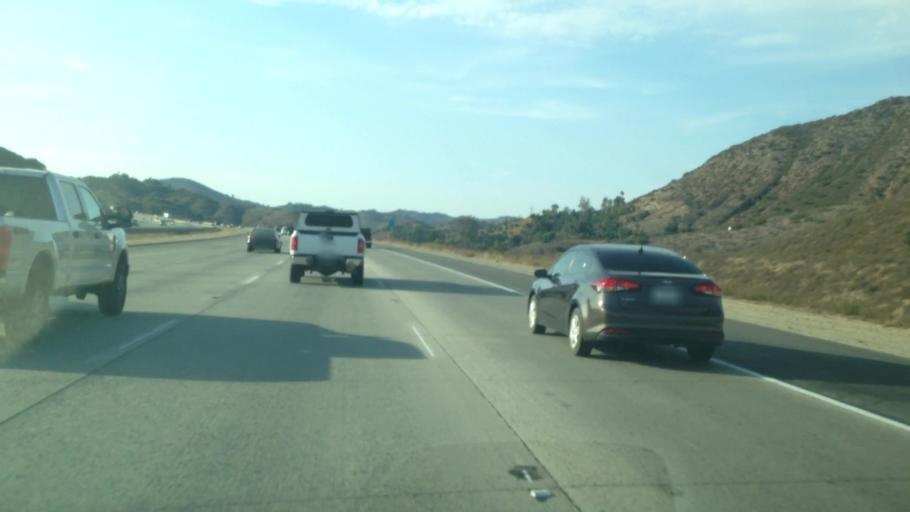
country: US
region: California
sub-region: San Diego County
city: Rainbow
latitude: 33.3595
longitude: -117.1590
